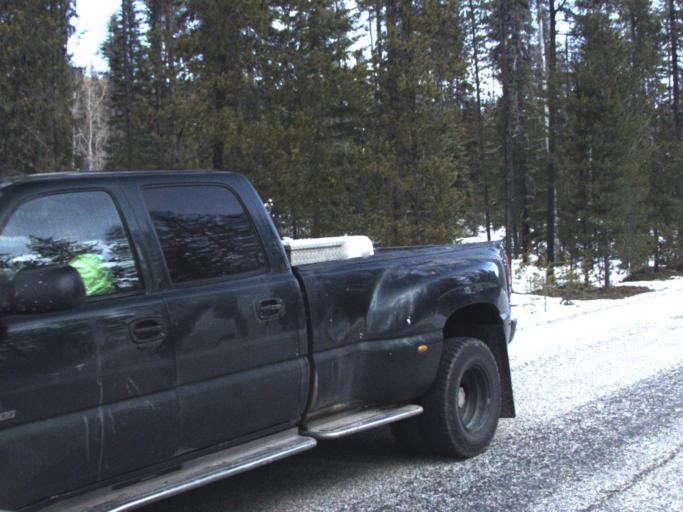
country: US
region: Washington
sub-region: Stevens County
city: Colville
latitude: 48.6517
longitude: -117.5021
